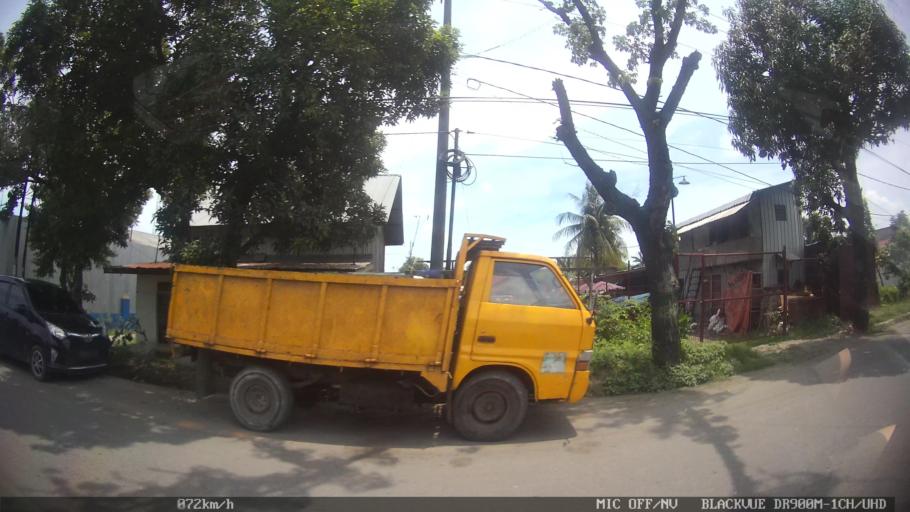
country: ID
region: North Sumatra
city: Labuhan Deli
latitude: 3.7107
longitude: 98.6798
